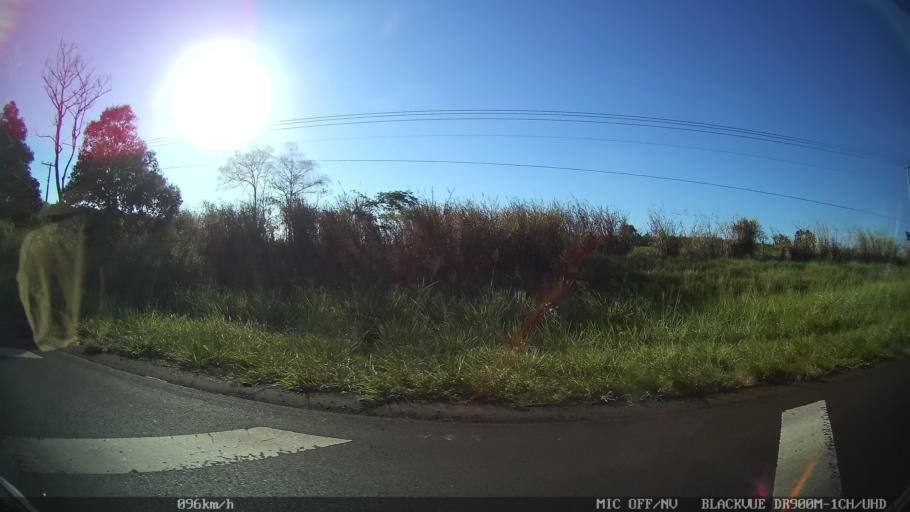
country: BR
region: Sao Paulo
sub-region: Olimpia
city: Olimpia
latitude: -20.7243
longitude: -49.0310
